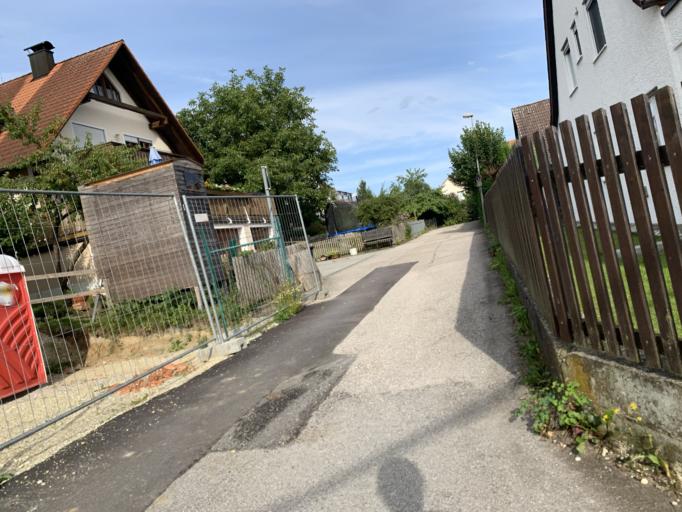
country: DE
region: Bavaria
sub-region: Upper Bavaria
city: Freising
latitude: 48.4031
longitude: 11.7176
